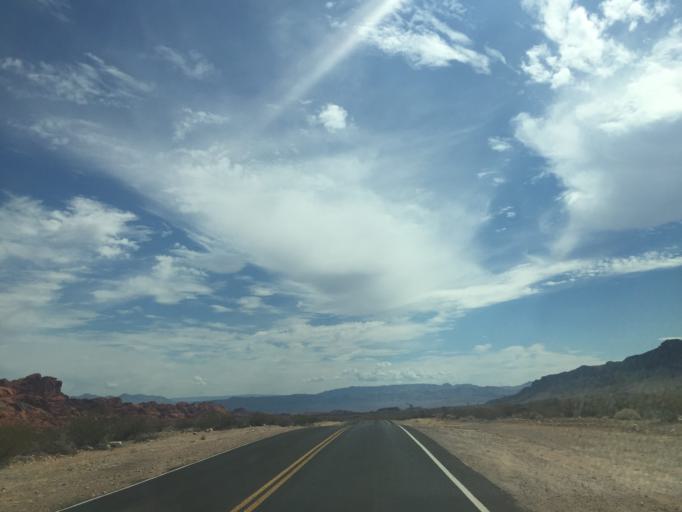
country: US
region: Nevada
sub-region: Clark County
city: Moapa Valley
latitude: 36.4260
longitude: -114.5393
